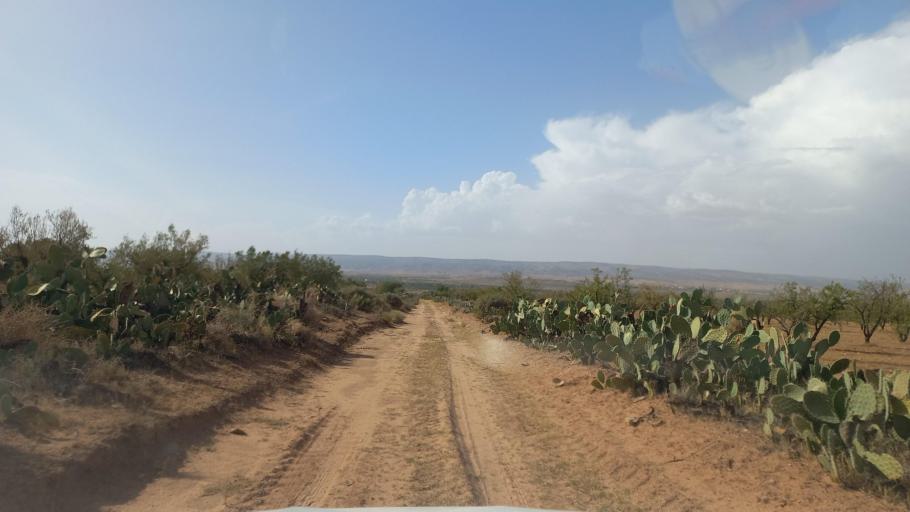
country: TN
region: Al Qasrayn
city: Kasserine
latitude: 35.2080
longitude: 8.9574
